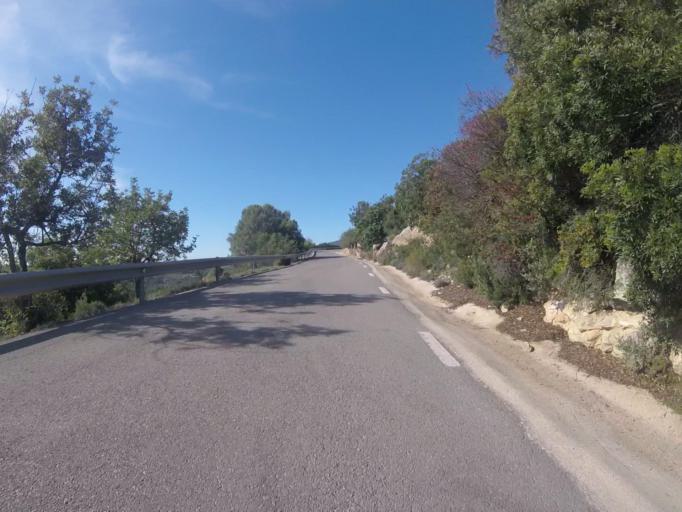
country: ES
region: Valencia
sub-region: Provincia de Castello
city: Sarratella
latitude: 40.2782
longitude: 0.0351
